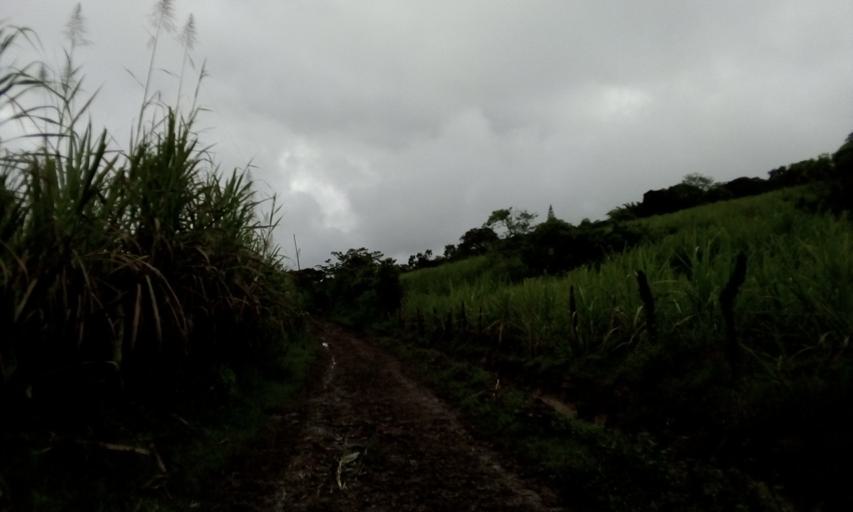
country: CO
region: Boyaca
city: Santana
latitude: 5.9979
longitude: -73.4988
